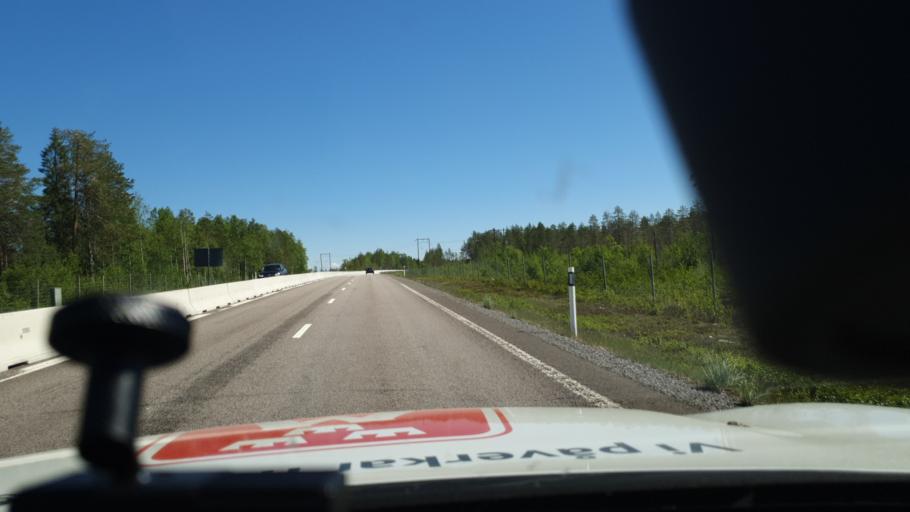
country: SE
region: Norrbotten
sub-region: Kalix Kommun
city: Toere
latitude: 65.9104
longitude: 22.8179
